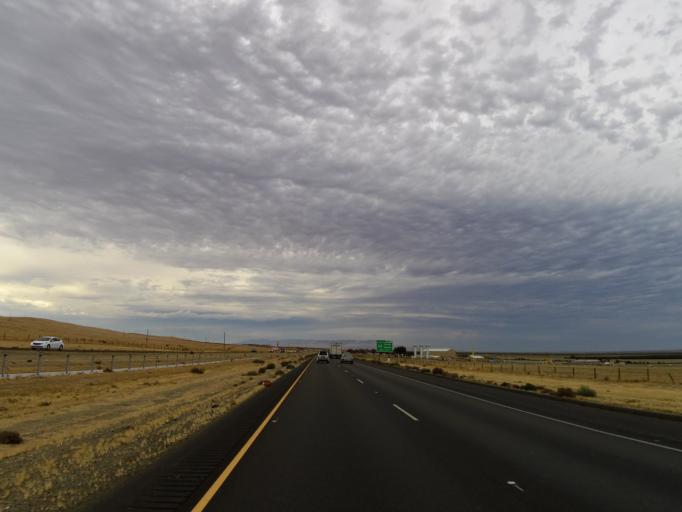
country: US
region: California
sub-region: Kings County
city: Avenal
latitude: 36.0667
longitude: -120.0851
